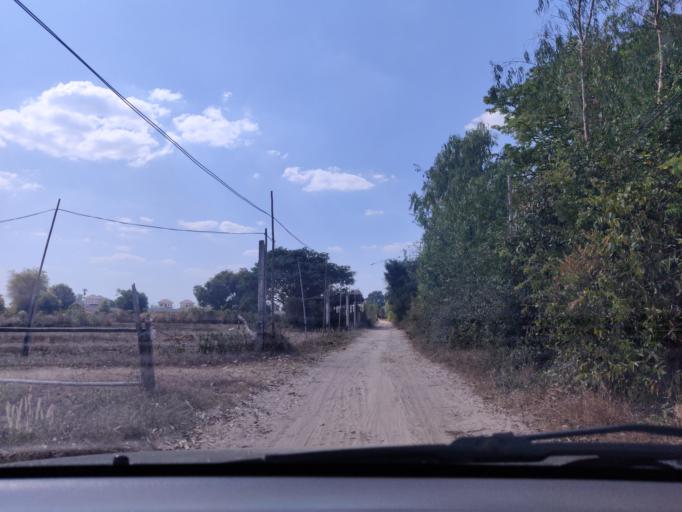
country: TH
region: Sisaket
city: Si Sa Ket
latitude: 15.1002
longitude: 104.3608
